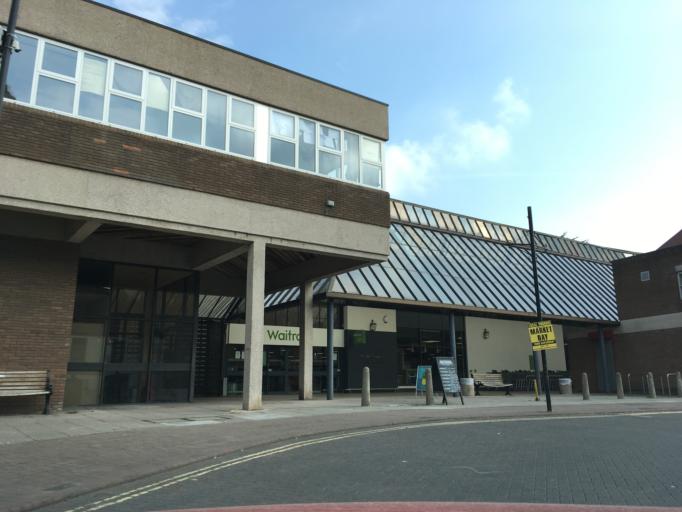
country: GB
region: England
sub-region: North Somerset
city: Nailsea
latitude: 51.4333
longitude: -2.7584
